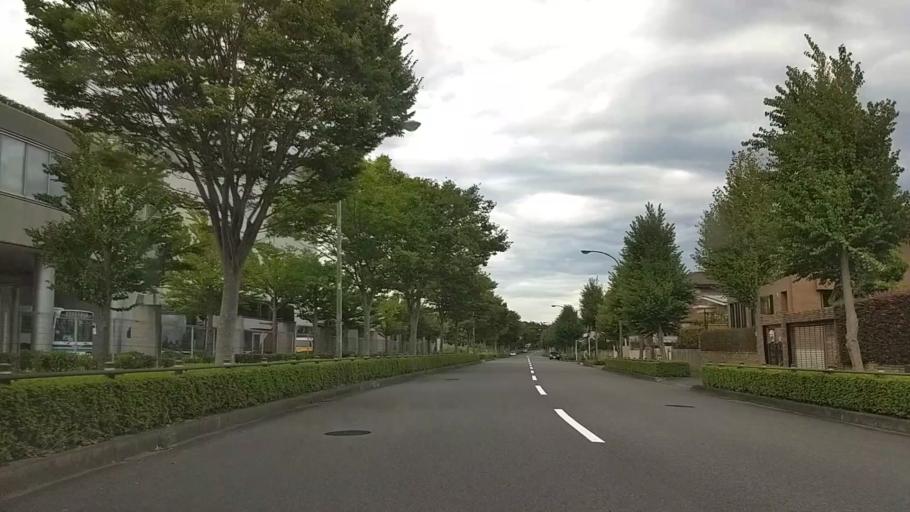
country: JP
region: Tokyo
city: Hachioji
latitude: 35.6265
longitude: 139.3169
